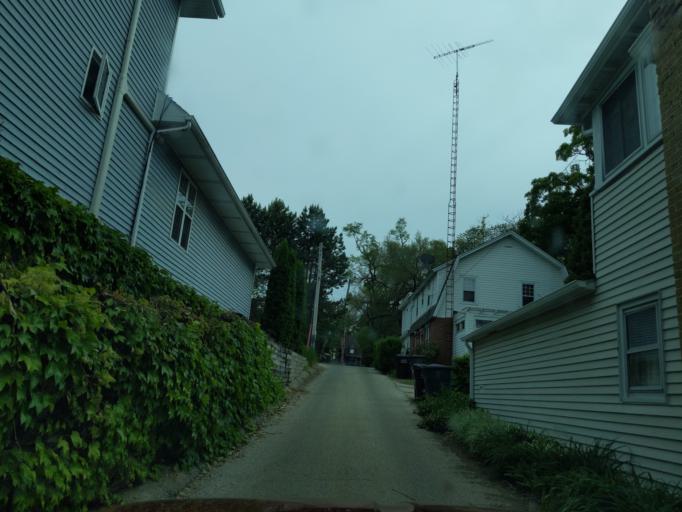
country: US
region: Wisconsin
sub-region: Walworth County
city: Lake Geneva
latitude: 42.5879
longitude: -88.4297
